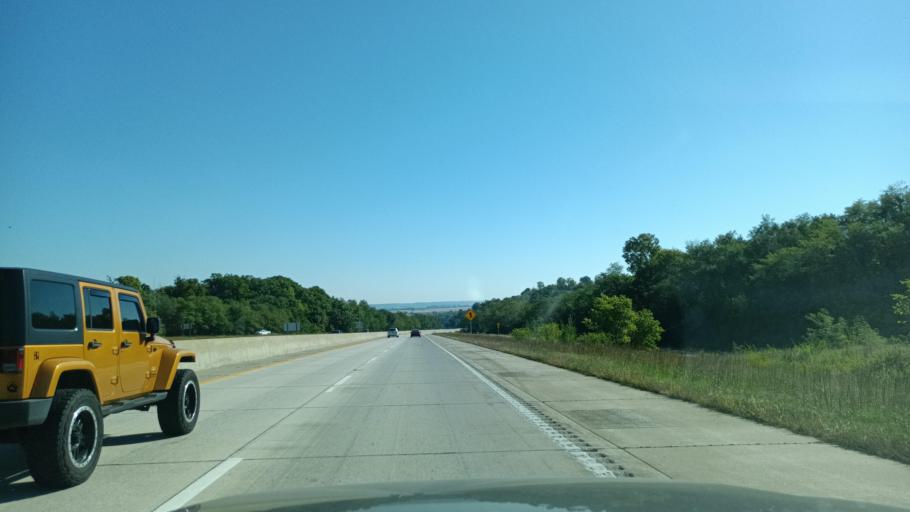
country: US
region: Missouri
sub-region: Marion County
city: Hannibal
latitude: 39.7184
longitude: -91.3722
